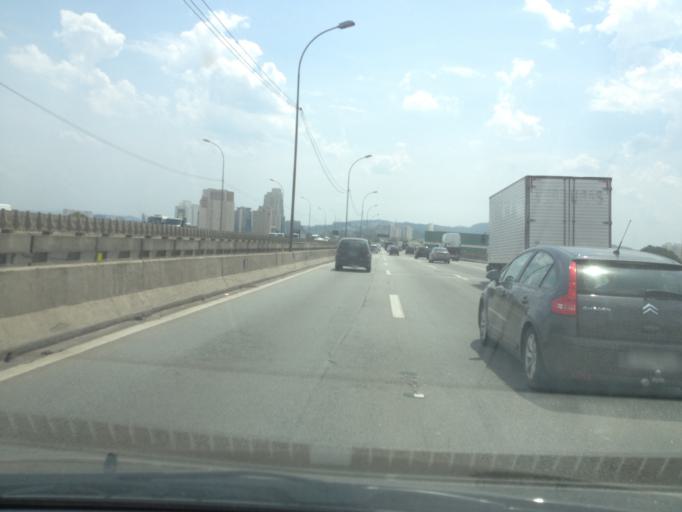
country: BR
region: Sao Paulo
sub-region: Barueri
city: Barueri
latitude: -23.5050
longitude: -46.8577
